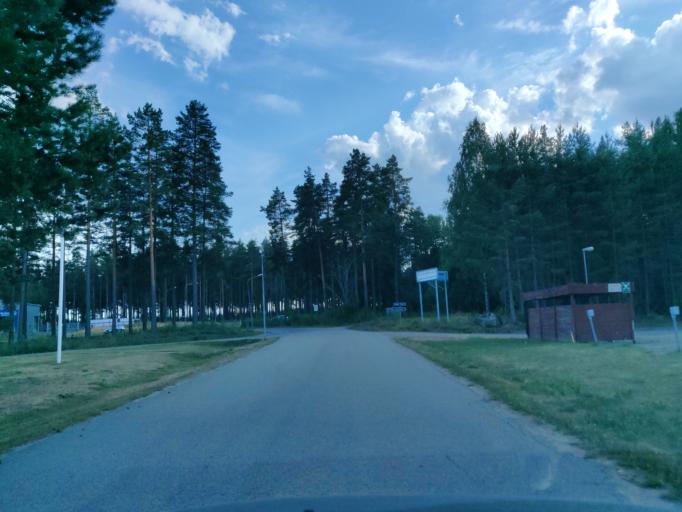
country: SE
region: Vaermland
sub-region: Hagfors Kommun
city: Hagfors
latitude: 60.0126
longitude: 13.6703
